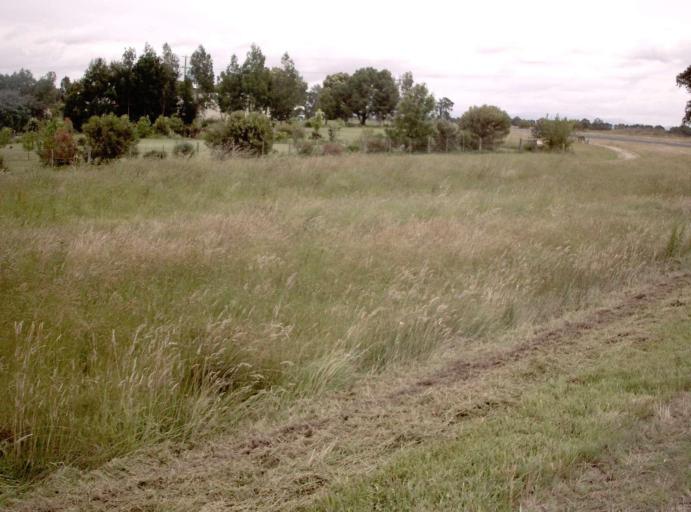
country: AU
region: Victoria
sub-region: Wellington
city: Sale
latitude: -37.9562
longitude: 147.0849
